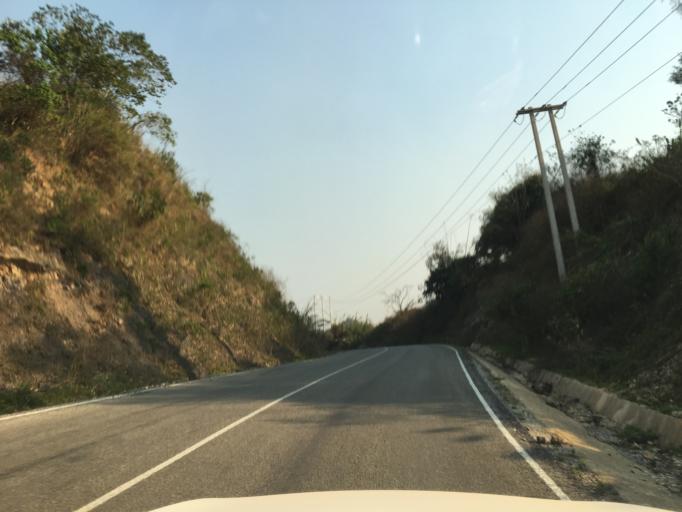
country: LA
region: Houaphan
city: Xam Nua
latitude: 20.5682
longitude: 104.0573
